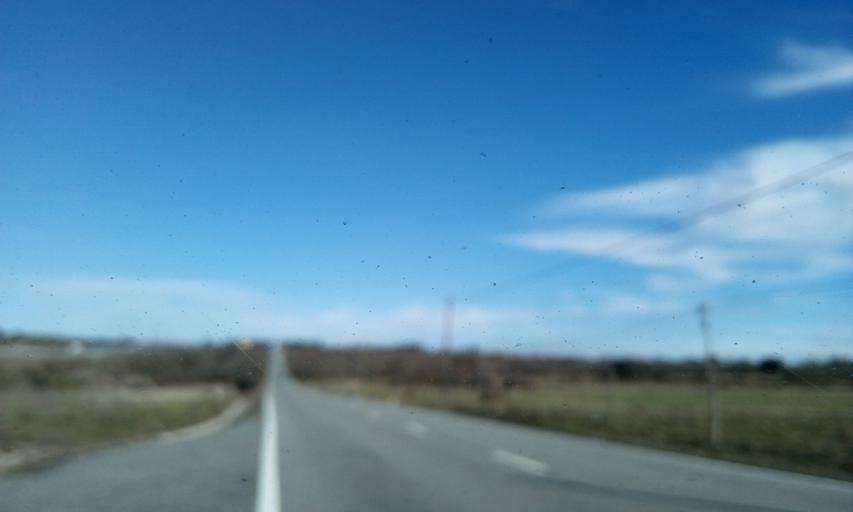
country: ES
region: Castille and Leon
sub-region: Provincia de Salamanca
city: Fuentes de Onoro
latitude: 40.6160
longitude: -6.8885
